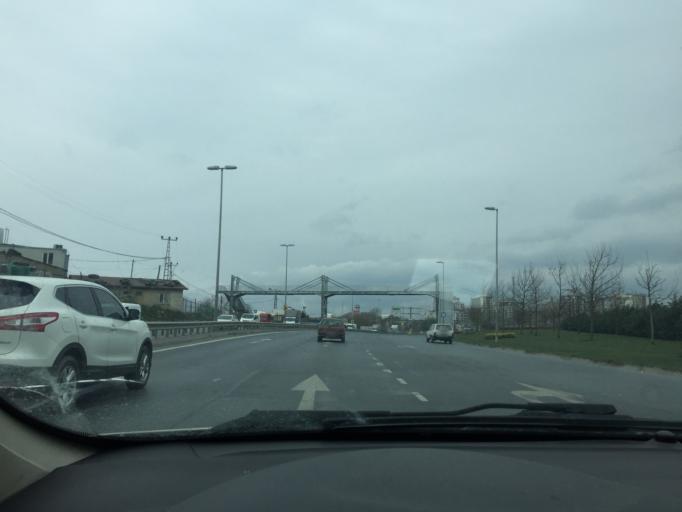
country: TR
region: Istanbul
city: Basaksehir
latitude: 41.1362
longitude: 28.8191
